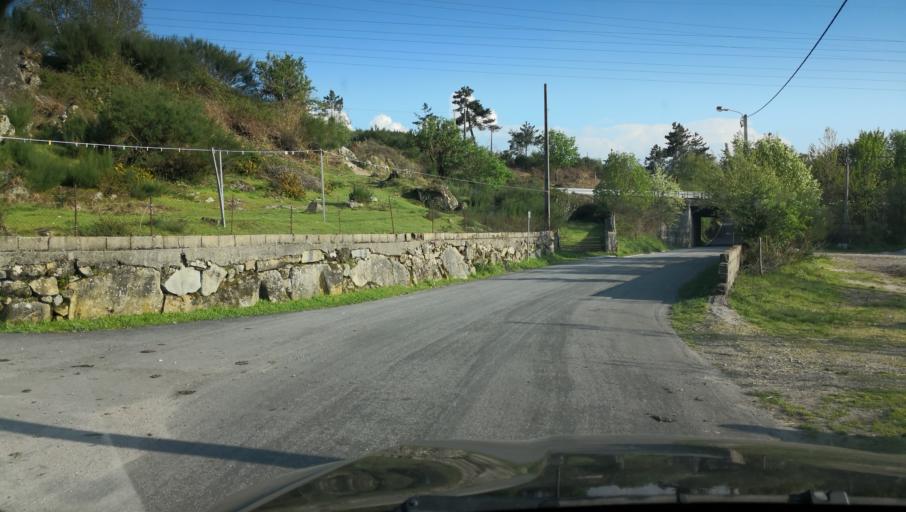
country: PT
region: Vila Real
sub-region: Santa Marta de Penaguiao
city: Santa Marta de Penaguiao
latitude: 41.2854
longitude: -7.8318
